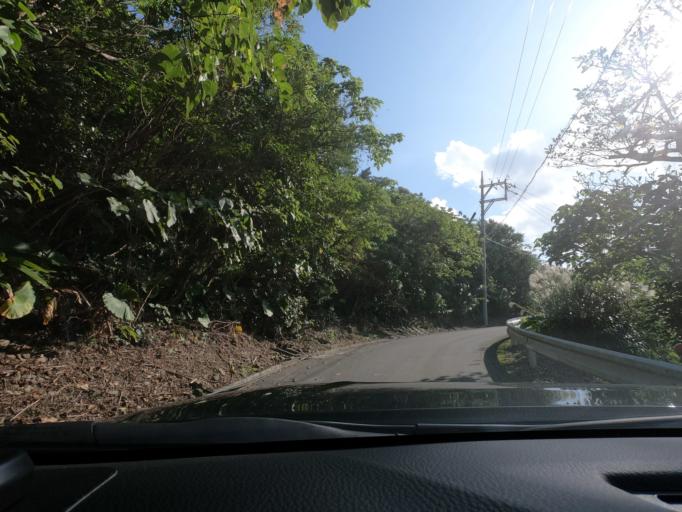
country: JP
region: Okinawa
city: Nago
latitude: 26.7570
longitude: 128.1942
